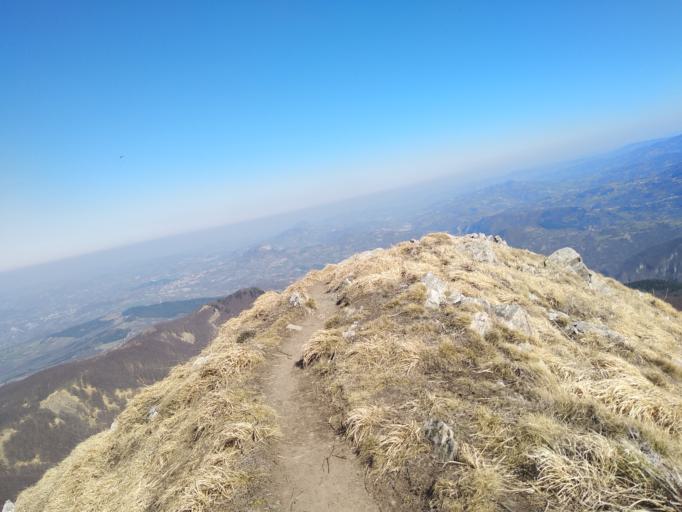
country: IT
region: Emilia-Romagna
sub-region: Provincia di Reggio Emilia
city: Busana
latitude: 44.3792
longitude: 10.2920
